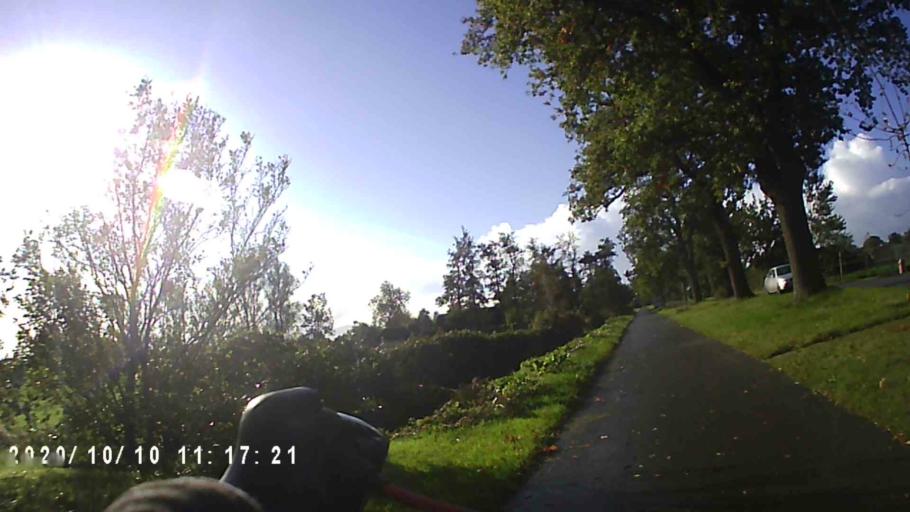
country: NL
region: Friesland
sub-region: Gemeente Smallingerland
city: Drachtstercompagnie
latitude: 53.0968
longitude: 6.1982
